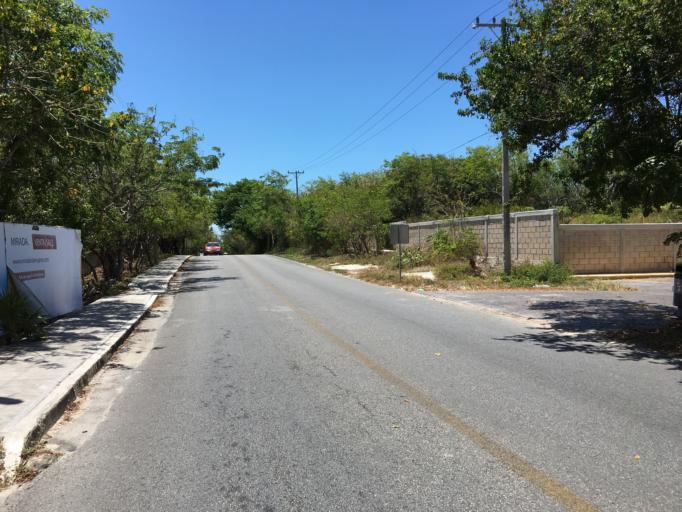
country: MX
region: Quintana Roo
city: Isla Mujeres
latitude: 21.2166
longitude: -86.7256
